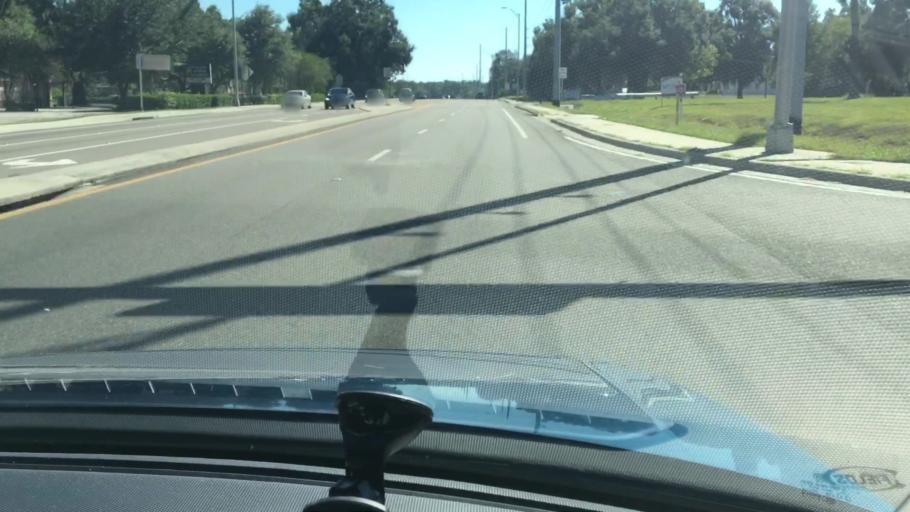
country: US
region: Florida
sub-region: Polk County
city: Kathleen
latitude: 28.1240
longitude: -82.0234
